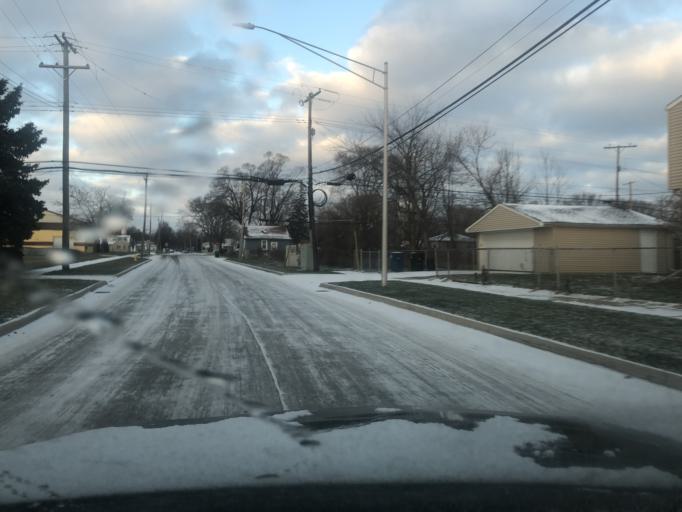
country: US
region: Michigan
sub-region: Wayne County
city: Garden City
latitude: 42.3001
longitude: -83.3477
